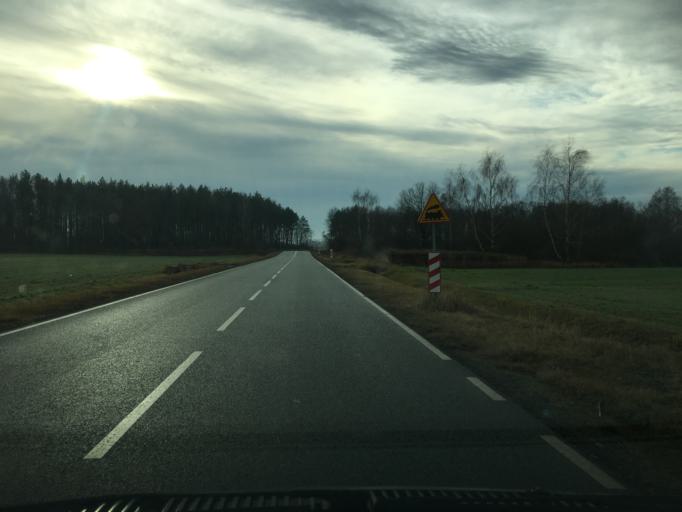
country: PL
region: Lower Silesian Voivodeship
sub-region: Powiat wroclawski
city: Dlugoleka
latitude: 51.1796
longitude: 17.2226
